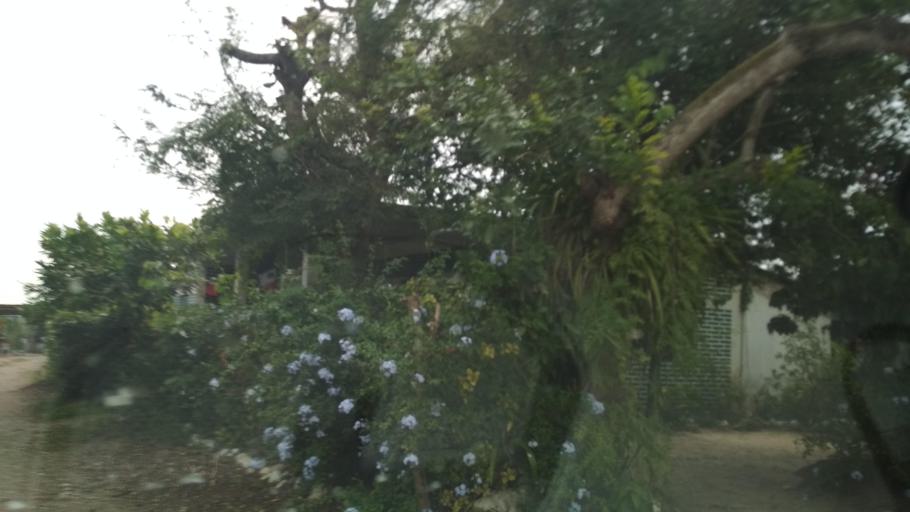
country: MM
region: Shan
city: Taunggyi
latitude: 20.3351
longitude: 97.3088
